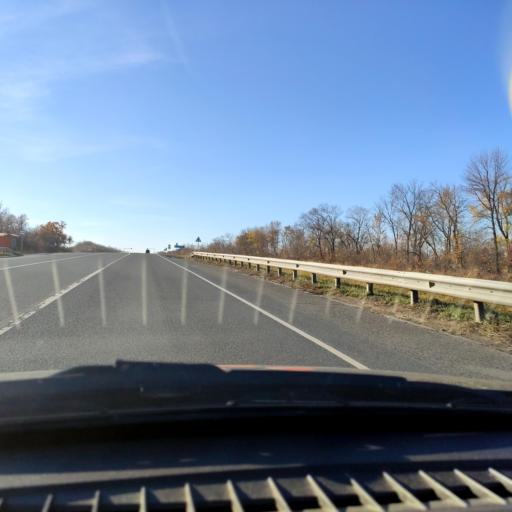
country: RU
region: Samara
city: Mezhdurechensk
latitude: 53.2577
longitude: 49.1097
